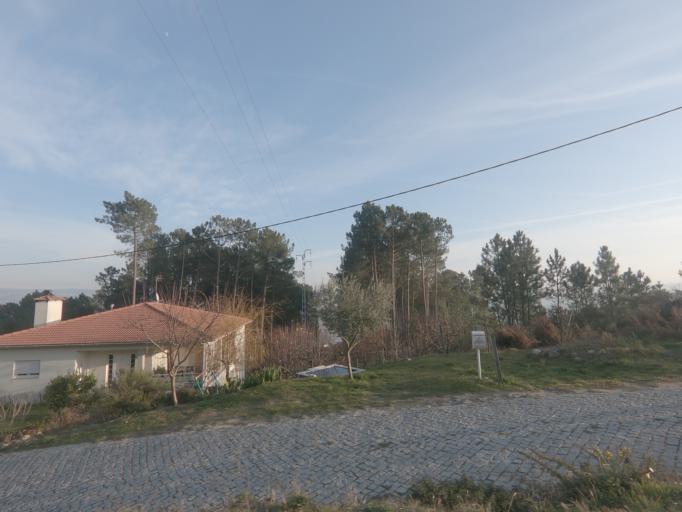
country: PT
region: Vila Real
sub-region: Vila Real
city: Vila Real
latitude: 41.3226
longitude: -7.7760
